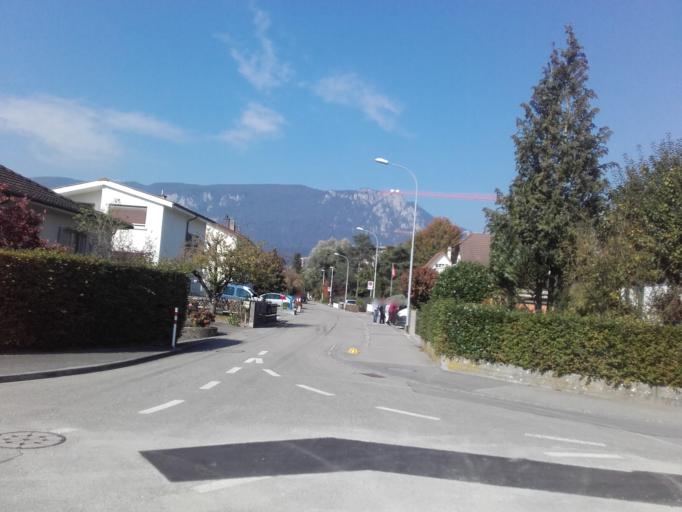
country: CH
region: Solothurn
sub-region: Bezirk Wasseramt
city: Zuchwil
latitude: 47.2114
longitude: 7.5618
